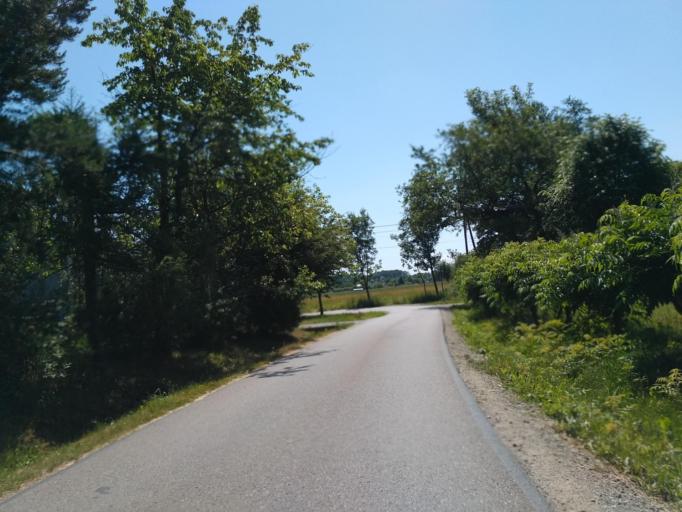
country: PL
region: Subcarpathian Voivodeship
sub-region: Powiat krosnienski
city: Odrzykon
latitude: 49.7247
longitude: 21.7700
